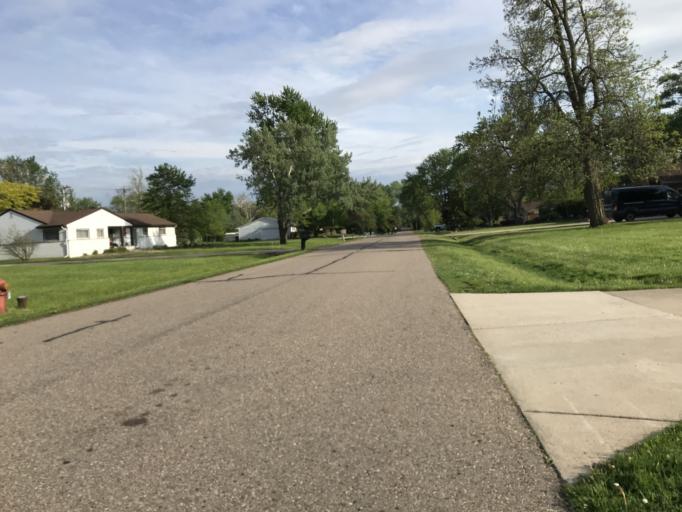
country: US
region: Michigan
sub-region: Oakland County
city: Farmington Hills
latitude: 42.4766
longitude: -83.3436
